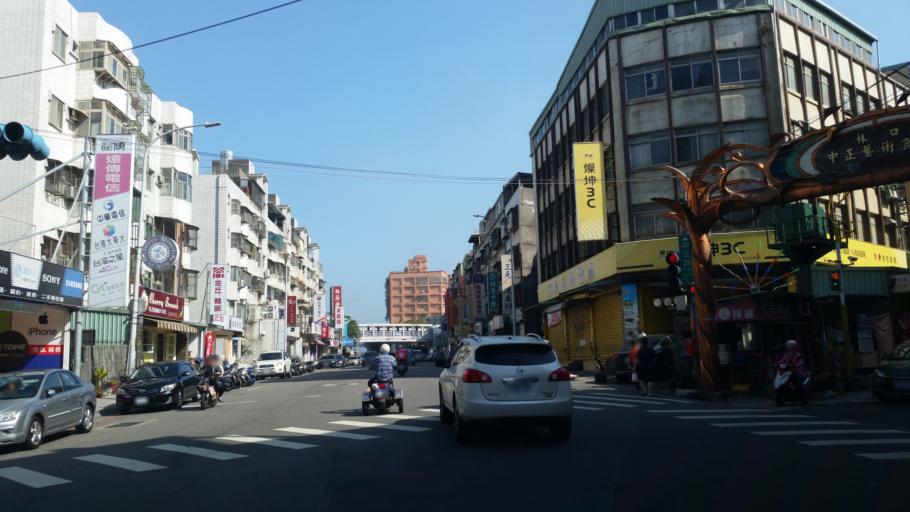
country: TW
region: Taipei
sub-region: Taipei
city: Banqiao
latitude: 25.0777
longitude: 121.3871
